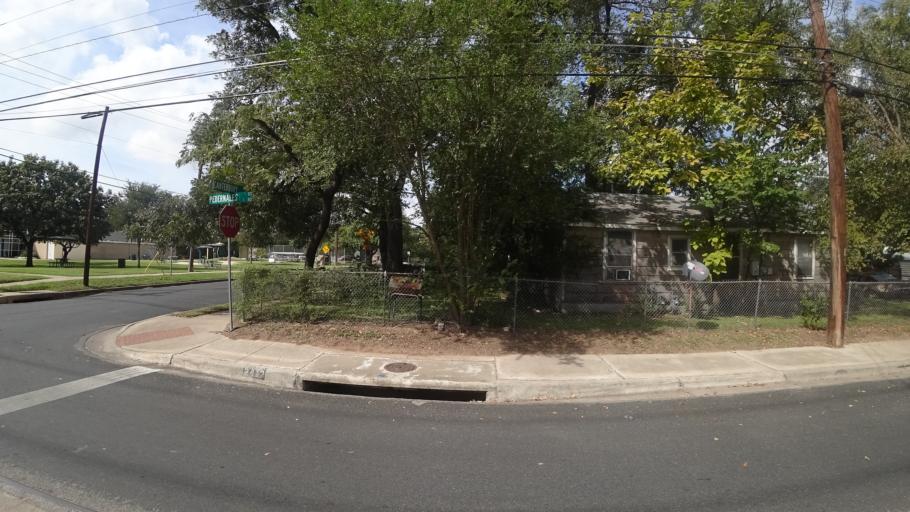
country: US
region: Texas
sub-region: Travis County
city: Austin
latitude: 30.2527
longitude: -97.7175
